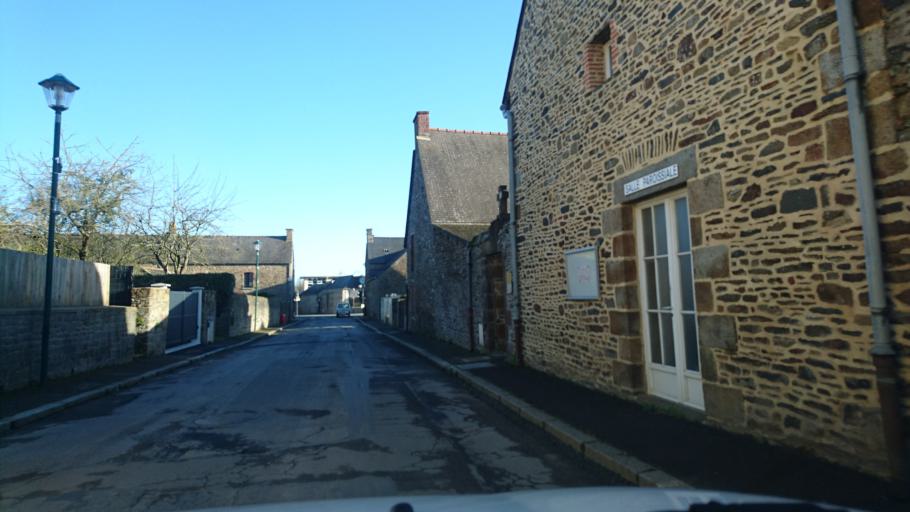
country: FR
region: Brittany
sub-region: Departement d'Ille-et-Vilaine
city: Baguer-Pican
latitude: 48.5523
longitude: -1.6992
